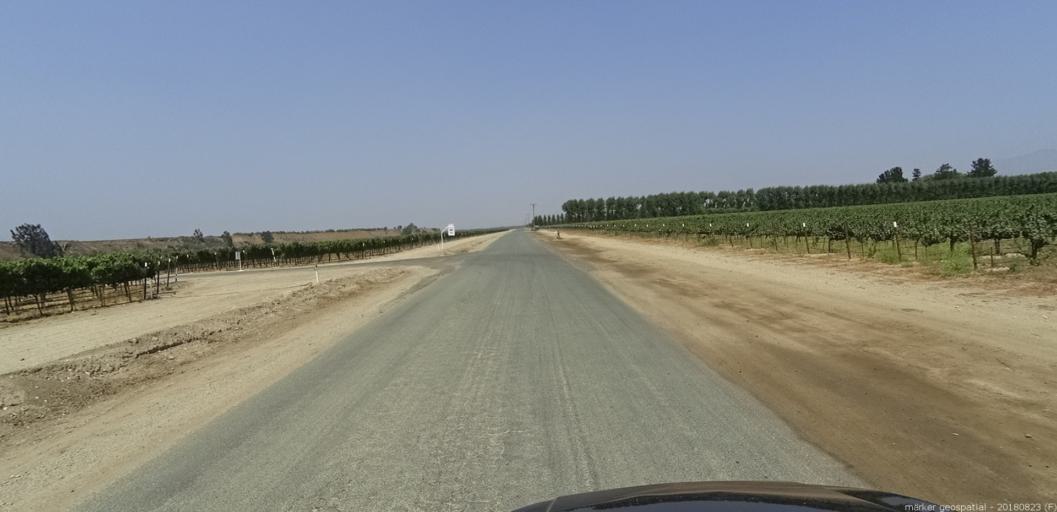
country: US
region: California
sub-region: Monterey County
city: Greenfield
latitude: 36.3425
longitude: -121.2979
